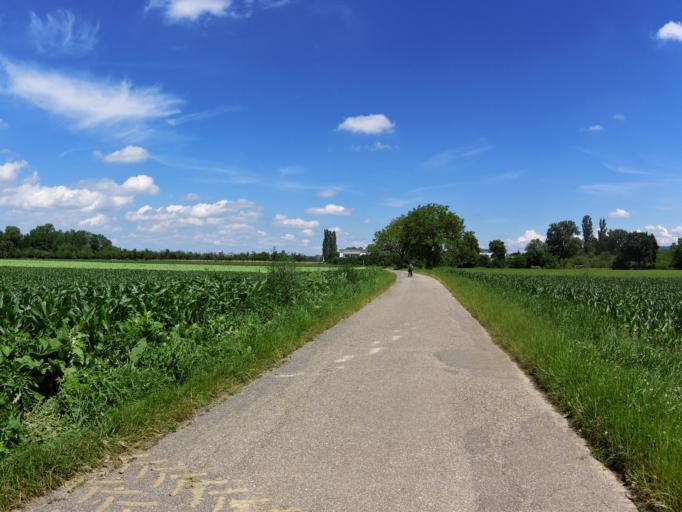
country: DE
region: Baden-Wuerttemberg
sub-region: Freiburg Region
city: Kippenheim
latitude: 48.3268
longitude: 7.8143
